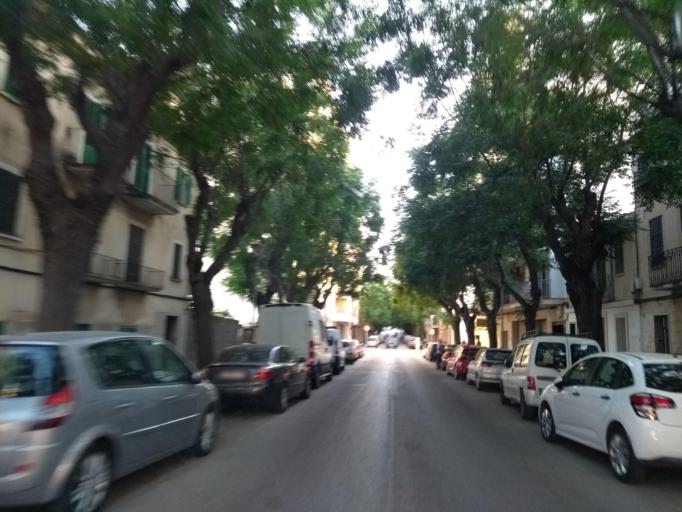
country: ES
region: Balearic Islands
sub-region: Illes Balears
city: Inca
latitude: 39.7235
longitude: 2.9158
